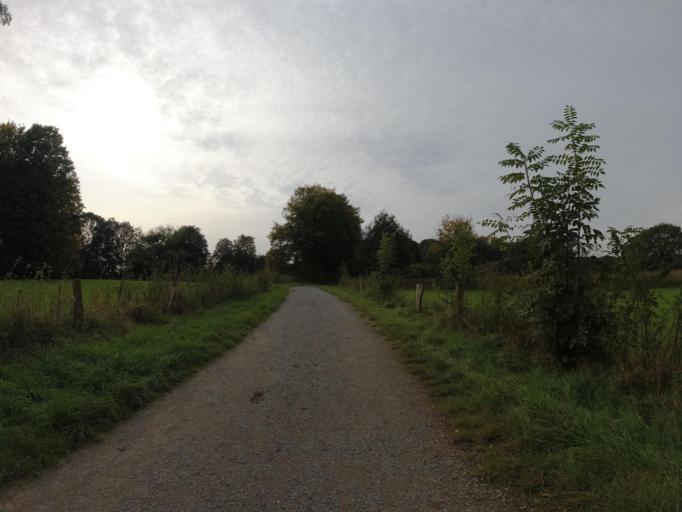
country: DE
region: North Rhine-Westphalia
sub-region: Regierungsbezirk Dusseldorf
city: Hochfeld
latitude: 51.3762
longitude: 6.6907
